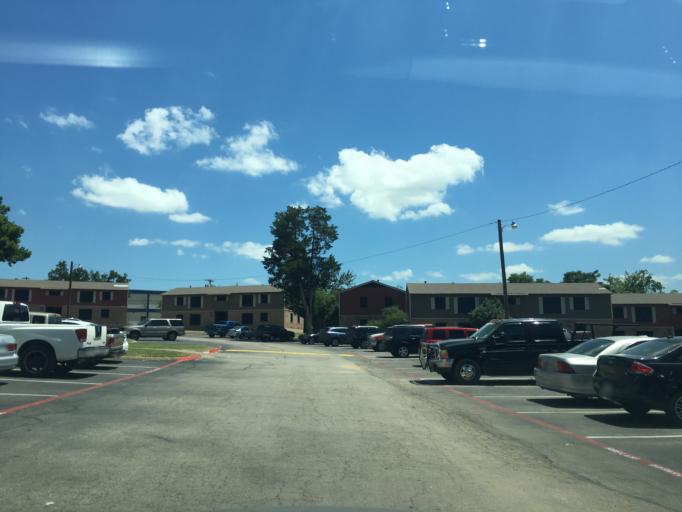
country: US
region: Texas
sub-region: Dallas County
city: Garland
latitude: 32.8472
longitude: -96.6890
